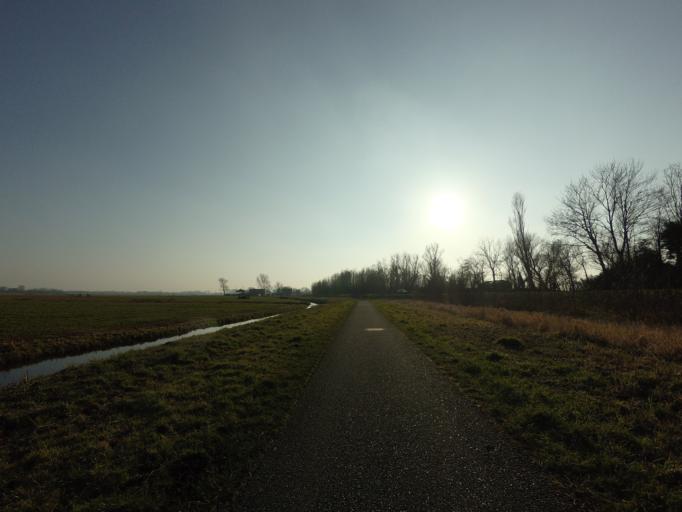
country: NL
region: North Holland
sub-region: Gemeente Haarlem
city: Haarlem
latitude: 52.4053
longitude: 4.6816
